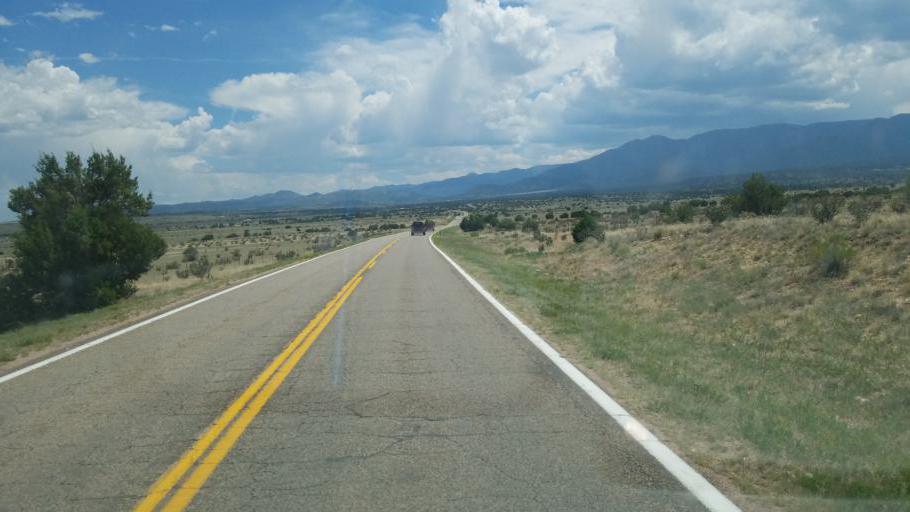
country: US
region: Colorado
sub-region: Fremont County
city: Florence
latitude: 38.3258
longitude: -105.1052
